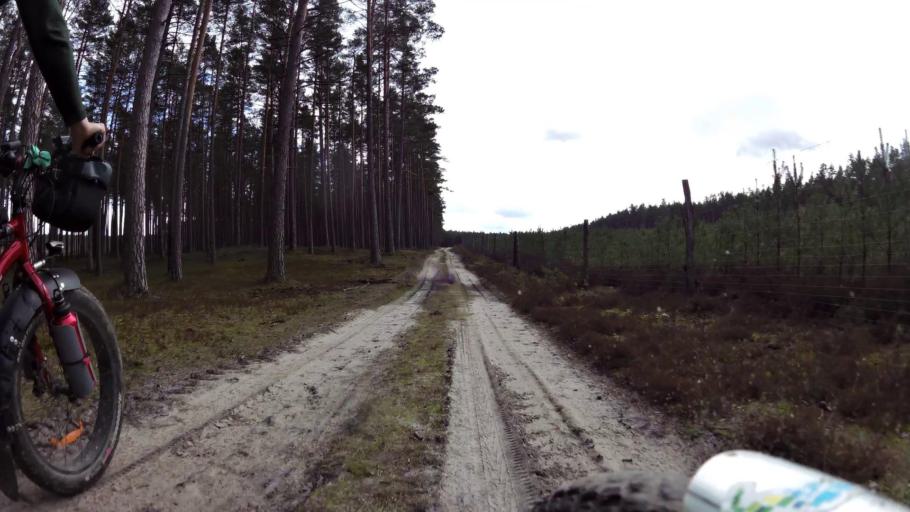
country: PL
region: Pomeranian Voivodeship
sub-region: Powiat bytowski
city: Kolczyglowy
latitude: 54.1624
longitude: 17.1883
